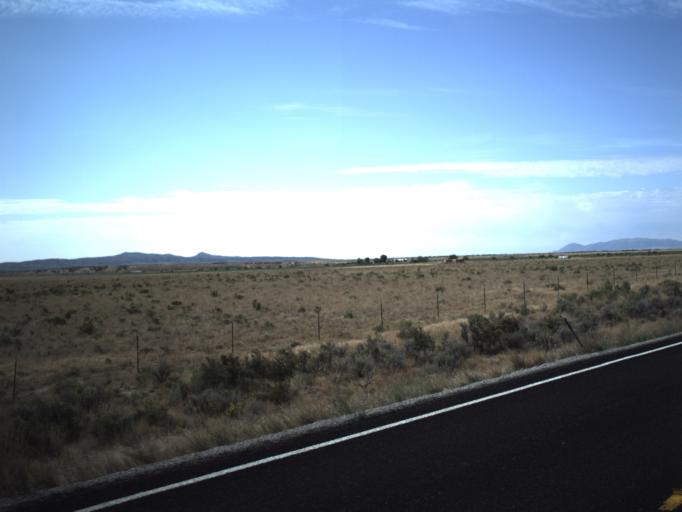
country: US
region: Idaho
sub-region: Cassia County
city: Burley
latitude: 41.7789
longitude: -113.4894
